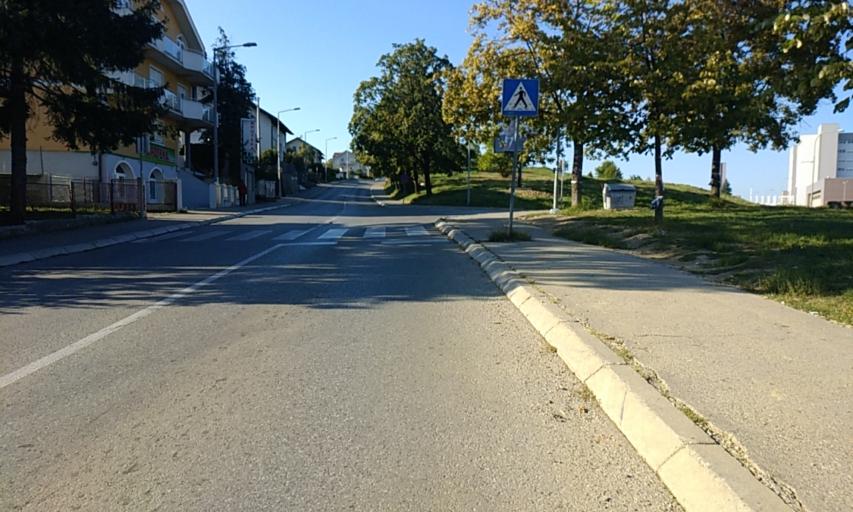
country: BA
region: Republika Srpska
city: Banja Luka
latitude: 44.7816
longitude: 17.1771
